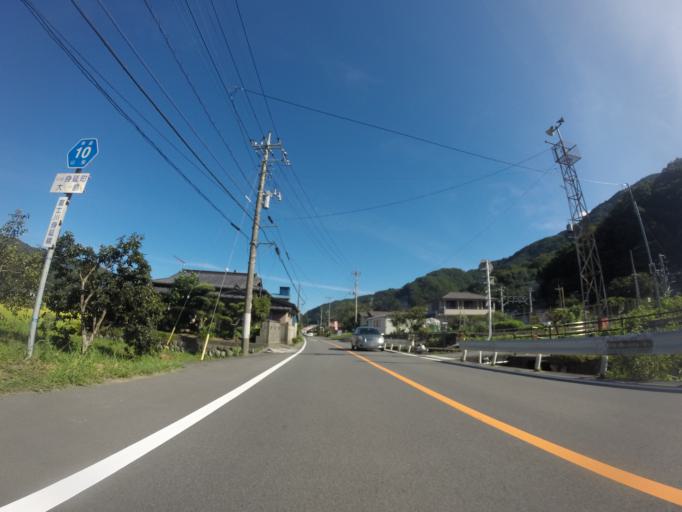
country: JP
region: Shizuoka
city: Fujinomiya
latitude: 35.3269
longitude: 138.4516
